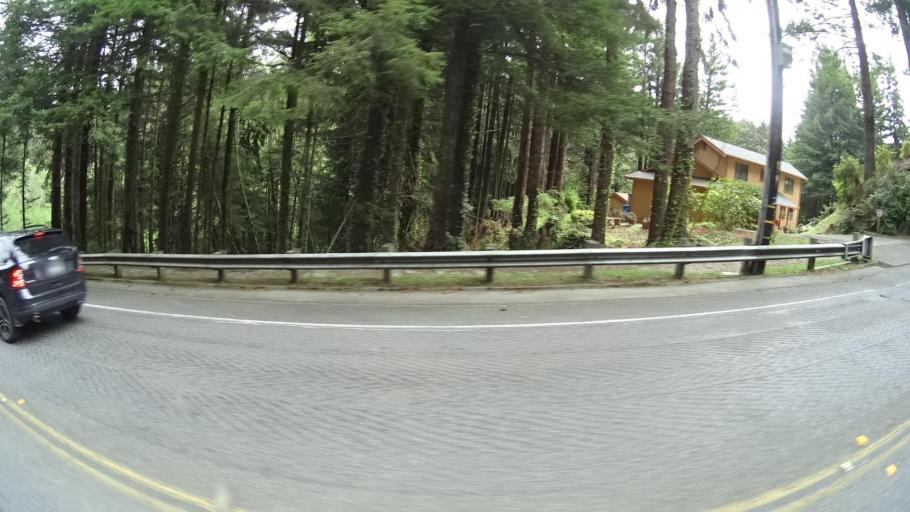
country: US
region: California
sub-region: Humboldt County
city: Cutten
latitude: 40.7665
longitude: -124.1548
